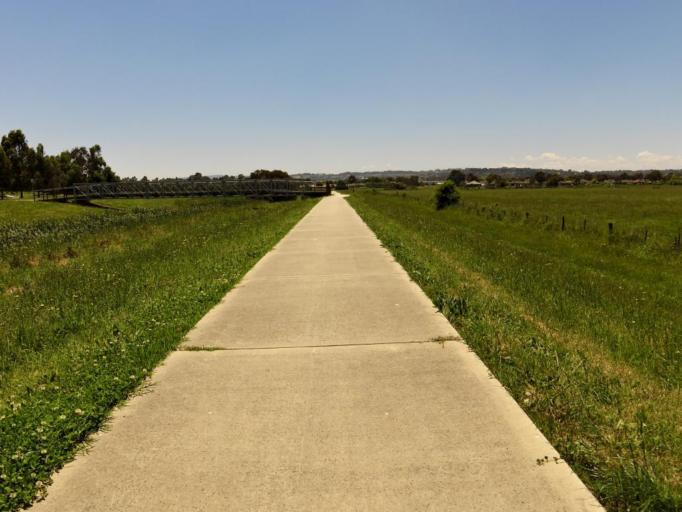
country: AU
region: Victoria
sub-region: Casey
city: Narre Warren
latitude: -38.0479
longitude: 145.3184
